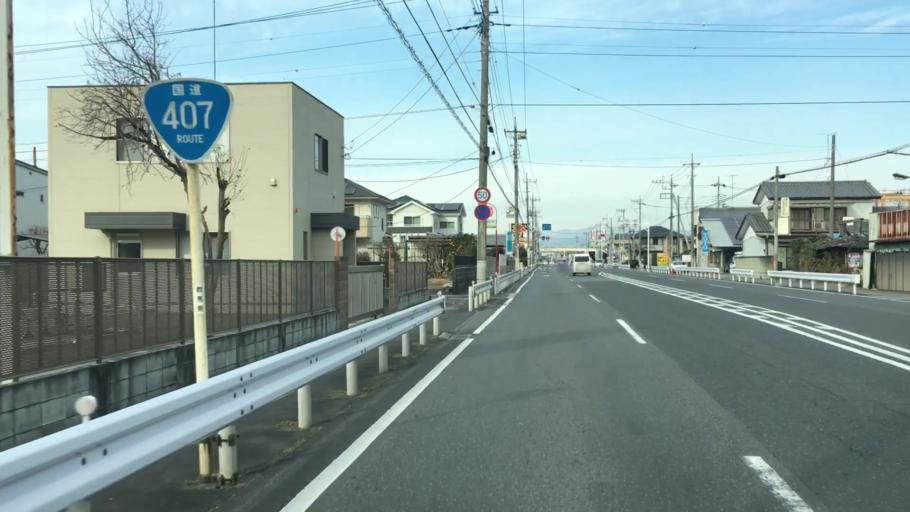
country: JP
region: Saitama
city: Menuma
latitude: 36.2527
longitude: 139.3784
